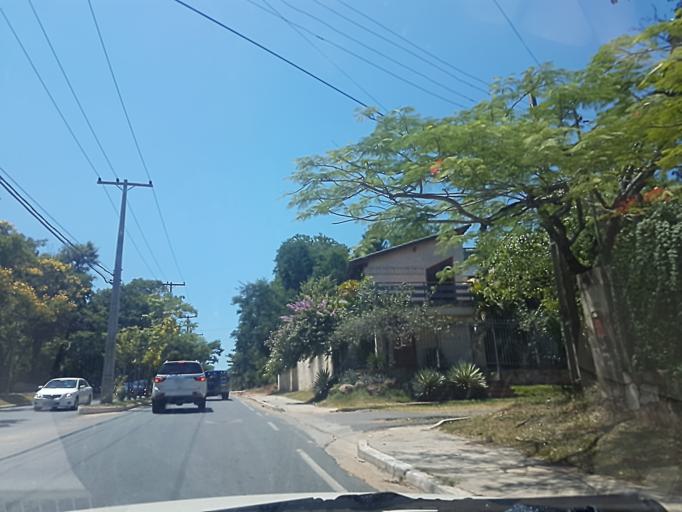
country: PY
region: Cordillera
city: San Bernardino
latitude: -25.3024
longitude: -57.3004
